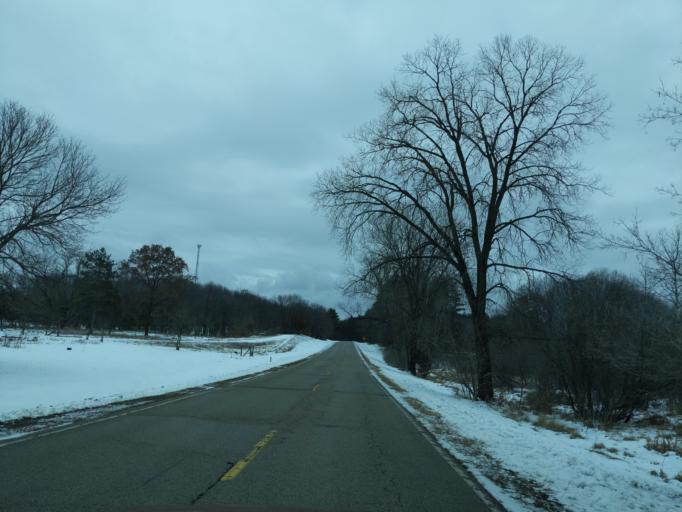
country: US
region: Wisconsin
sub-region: Marquette County
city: Montello
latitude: 43.9151
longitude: -89.3397
